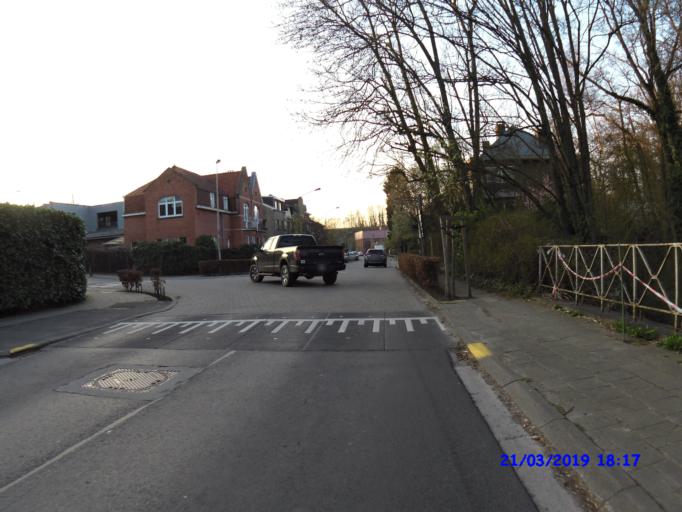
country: BE
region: Flanders
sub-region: Provincie Vlaams-Brabant
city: Linkebeek
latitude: 50.7753
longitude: 4.3313
